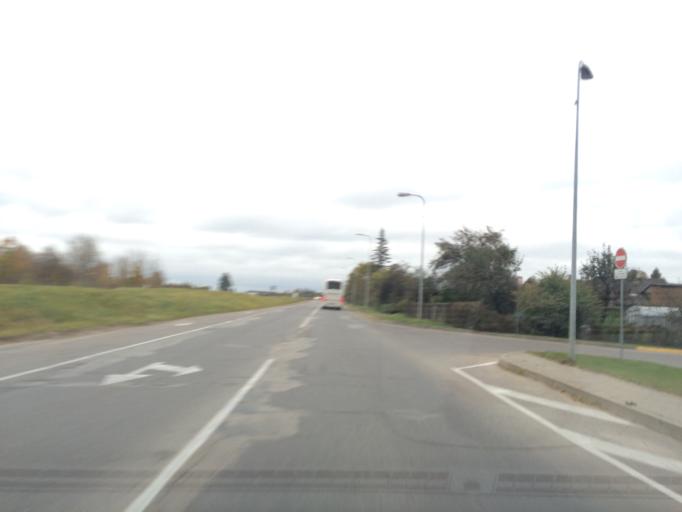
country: LV
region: Jekabpils Rajons
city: Jekabpils
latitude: 56.5104
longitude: 25.8744
